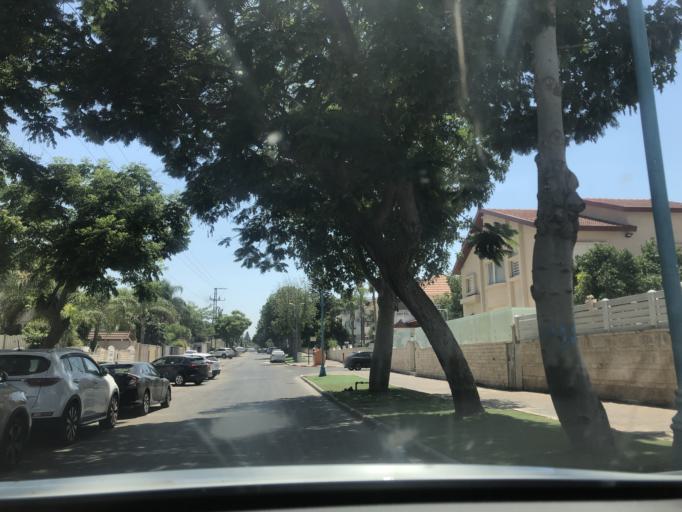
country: IL
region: Central District
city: Lod
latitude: 31.9407
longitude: 34.8910
